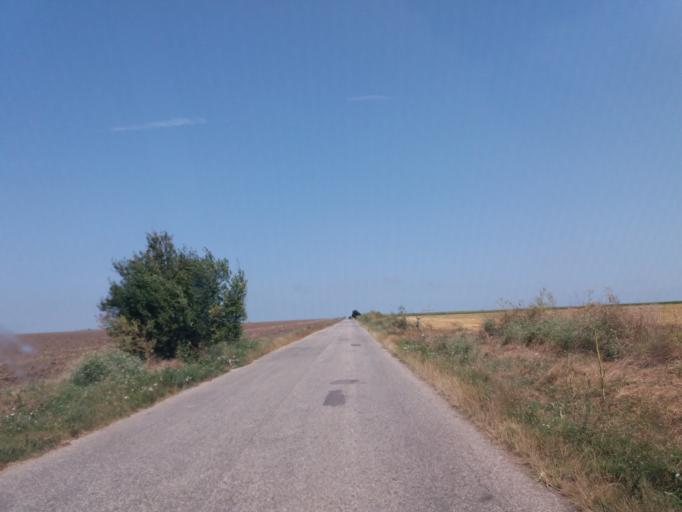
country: RO
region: Constanta
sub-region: Comuna Corbu
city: Corbu
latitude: 44.4240
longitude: 28.6730
